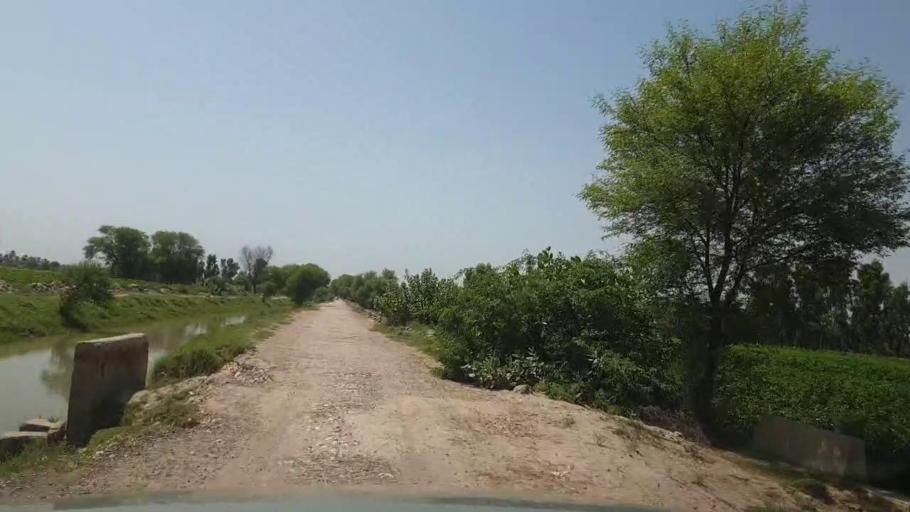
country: PK
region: Sindh
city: Rohri
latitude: 27.6564
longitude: 68.9825
